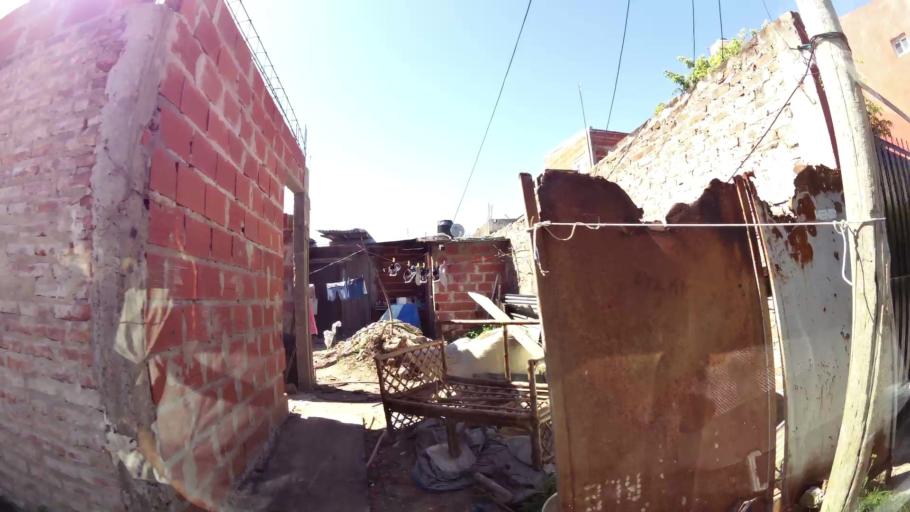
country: AR
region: Buenos Aires
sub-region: Partido de Quilmes
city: Quilmes
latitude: -34.6870
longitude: -58.3027
